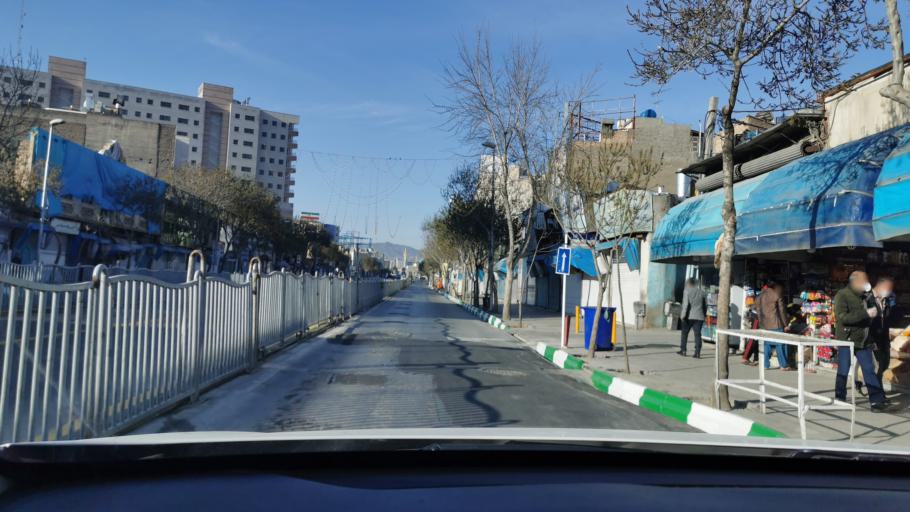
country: IR
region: Razavi Khorasan
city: Mashhad
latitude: 36.2938
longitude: 59.6248
